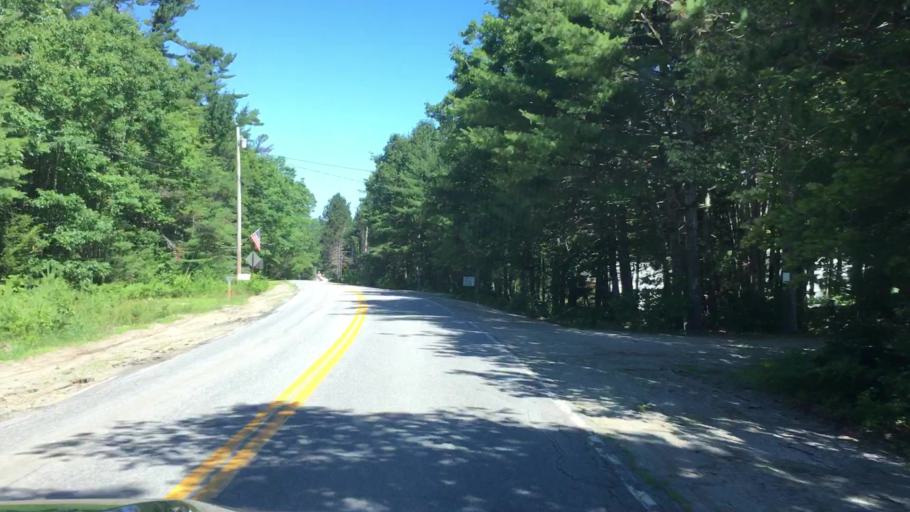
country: US
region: Maine
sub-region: Hancock County
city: Penobscot
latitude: 44.4478
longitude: -68.7018
